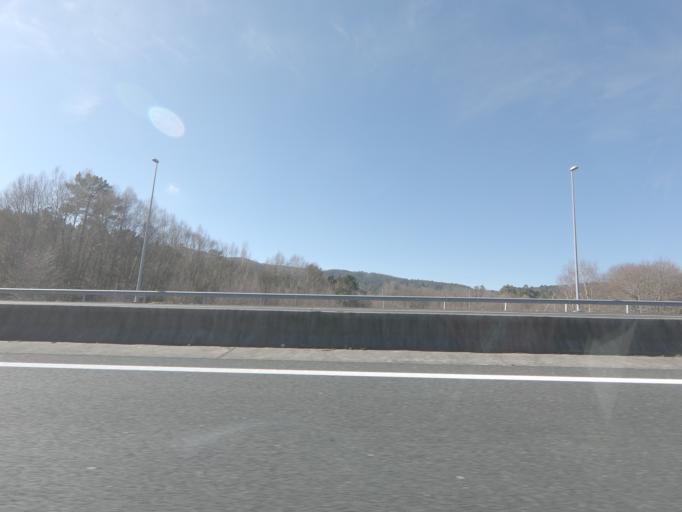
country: ES
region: Galicia
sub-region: Provincia de Ourense
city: Pinor
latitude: 42.5204
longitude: -8.0193
